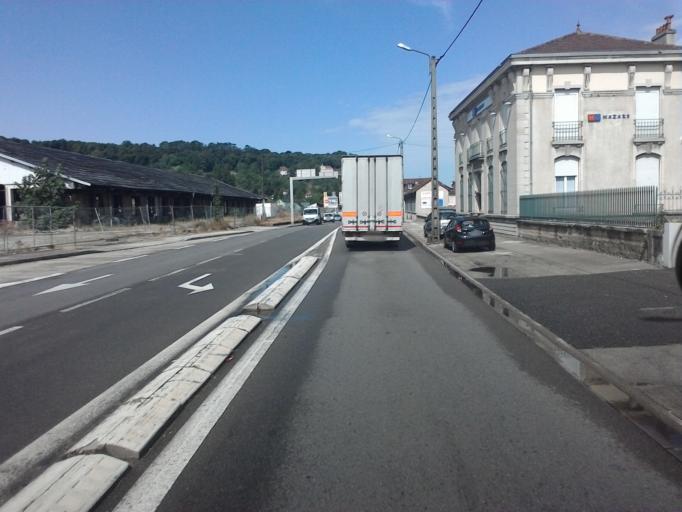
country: FR
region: Franche-Comte
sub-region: Departement du Jura
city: Lons-le-Saunier
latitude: 46.6690
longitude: 5.5499
